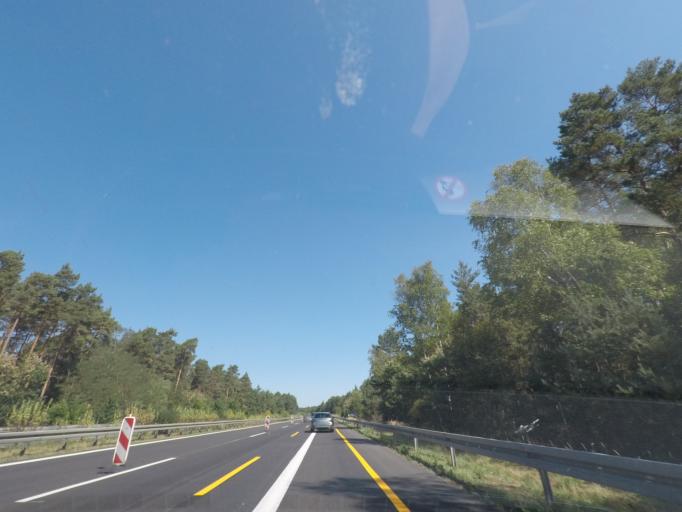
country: DE
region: Brandenburg
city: Bronkow
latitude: 51.6384
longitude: 13.9418
